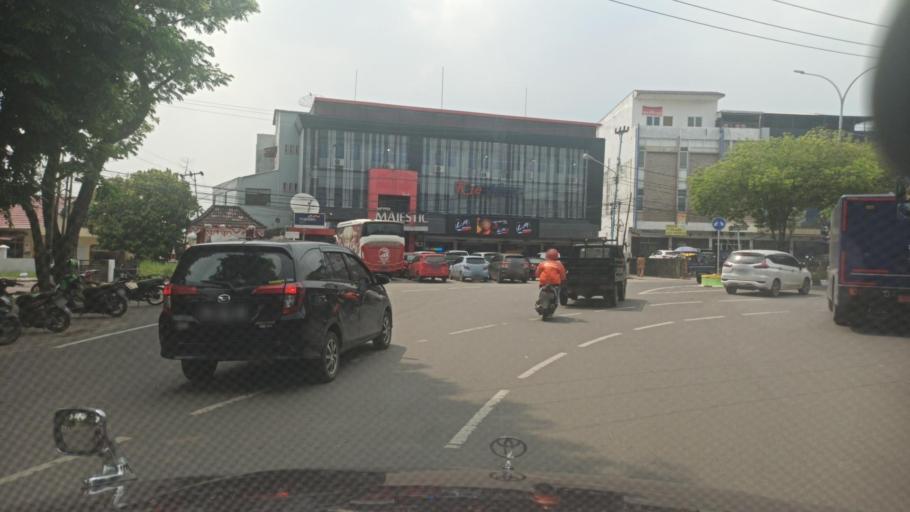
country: ID
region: South Sumatra
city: Palembang
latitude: -2.9764
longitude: 104.7377
